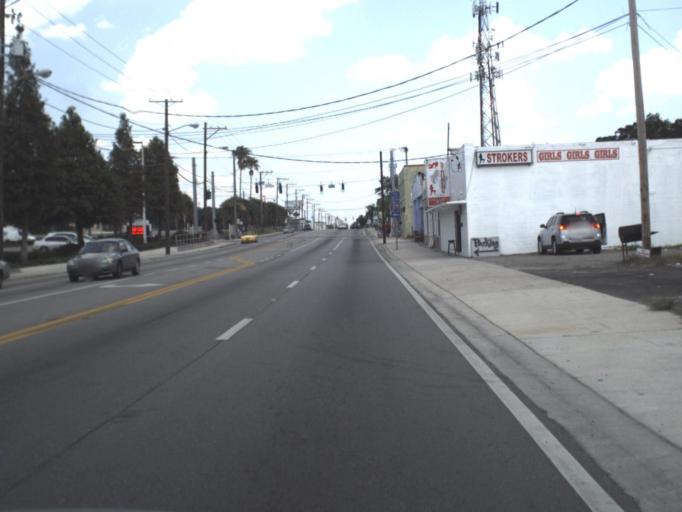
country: US
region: Florida
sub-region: Hillsborough County
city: University
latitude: 28.0214
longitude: -82.4512
